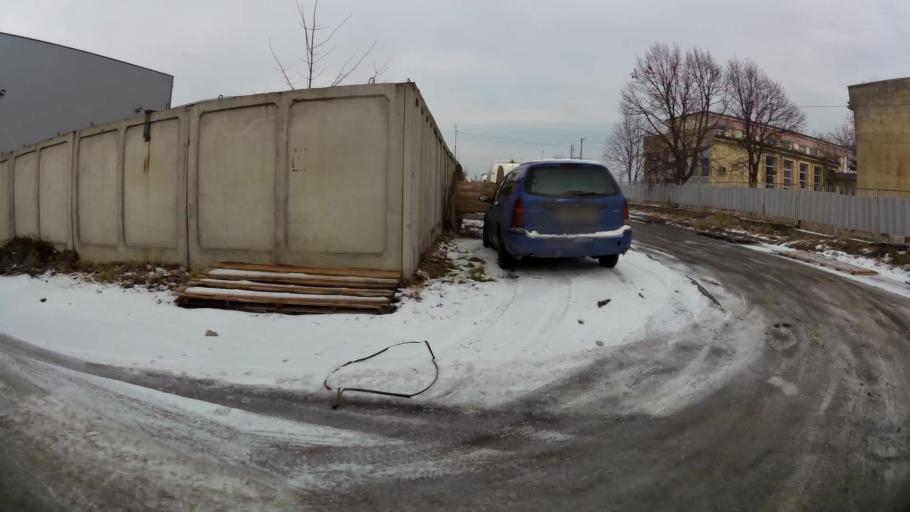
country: BG
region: Sofia-Capital
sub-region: Stolichna Obshtina
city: Sofia
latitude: 42.7069
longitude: 23.4130
